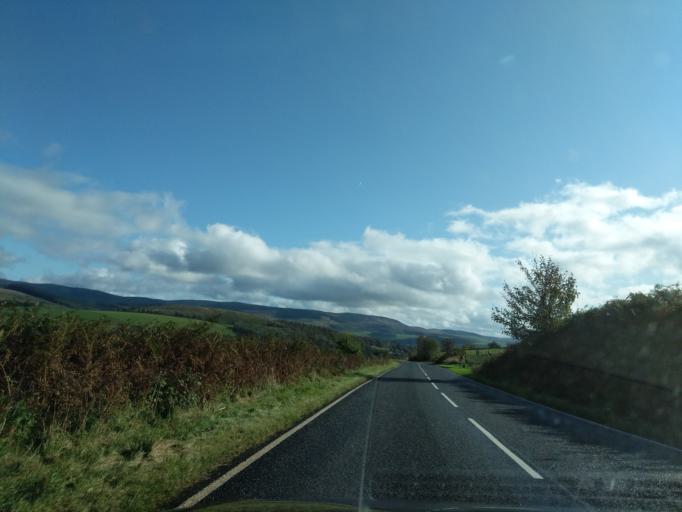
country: GB
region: Scotland
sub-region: Dumfries and Galloway
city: Moffat
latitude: 55.3542
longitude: -3.4685
